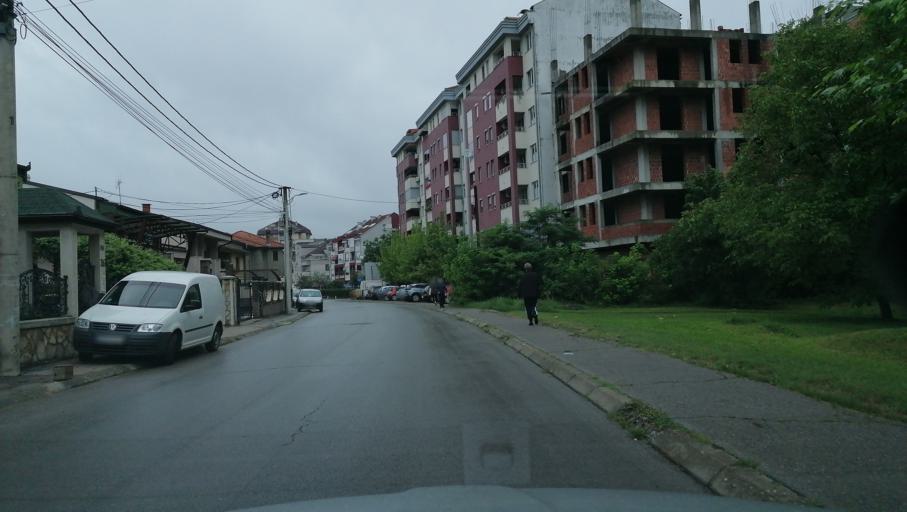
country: RS
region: Central Serbia
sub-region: Rasinski Okrug
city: Krusevac
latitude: 43.5687
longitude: 21.3295
